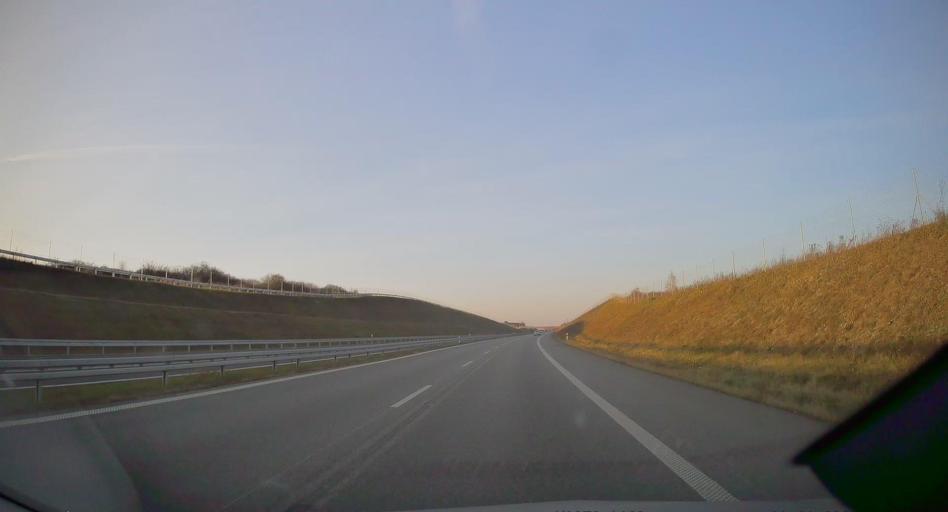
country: PL
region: Silesian Voivodeship
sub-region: Powiat bedzinski
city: Mierzecice
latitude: 50.4316
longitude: 19.1523
